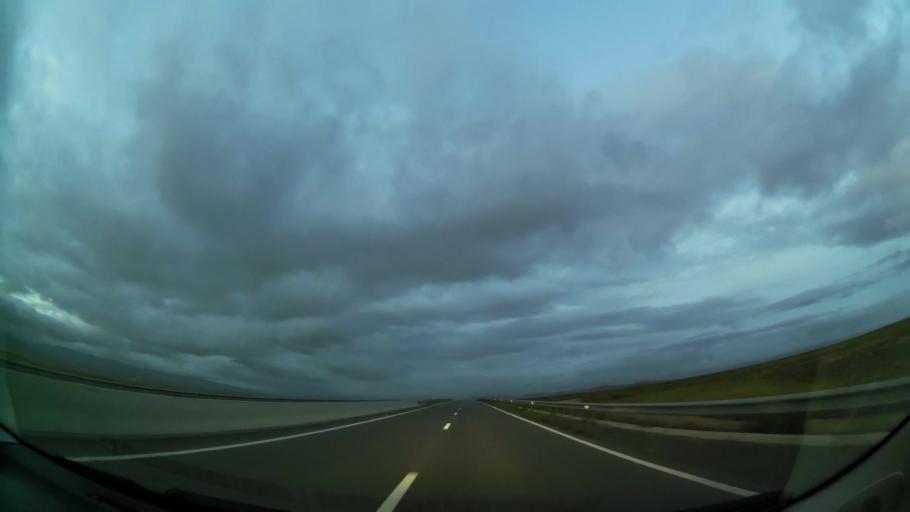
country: MA
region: Oriental
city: El Aioun
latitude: 34.6297
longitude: -2.3520
